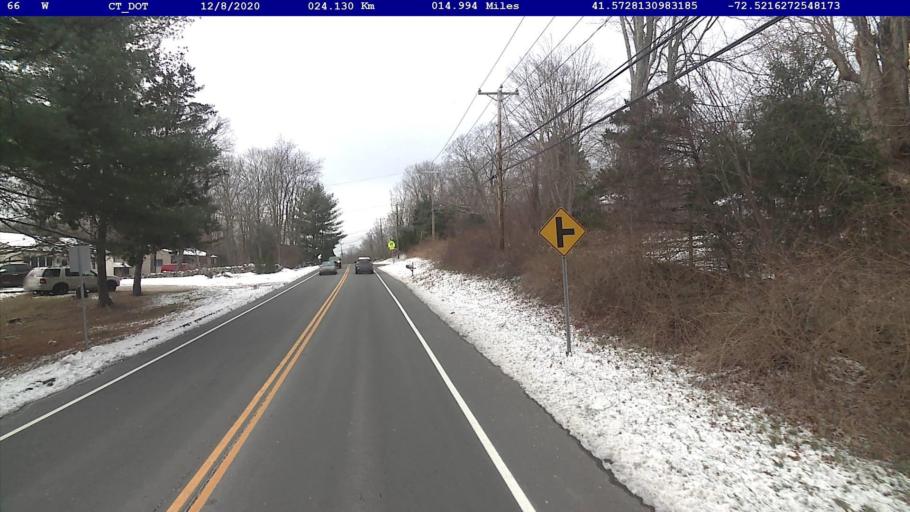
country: US
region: Connecticut
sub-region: Middlesex County
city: East Hampton
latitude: 41.5728
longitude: -72.5216
